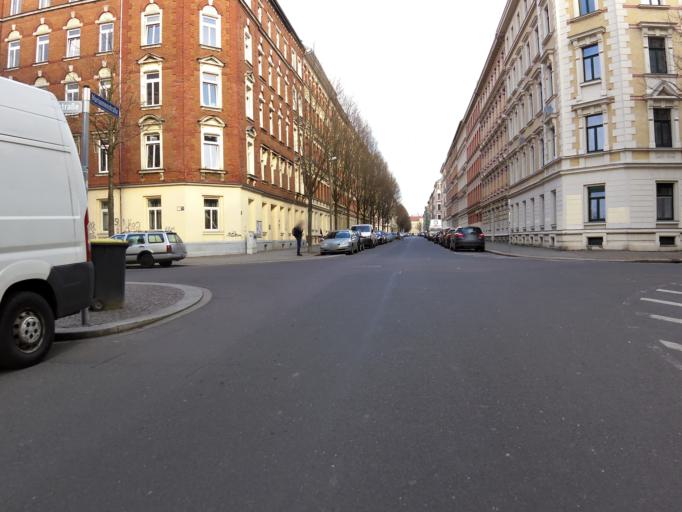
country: DE
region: Saxony
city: Leipzig
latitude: 51.3468
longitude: 12.4072
